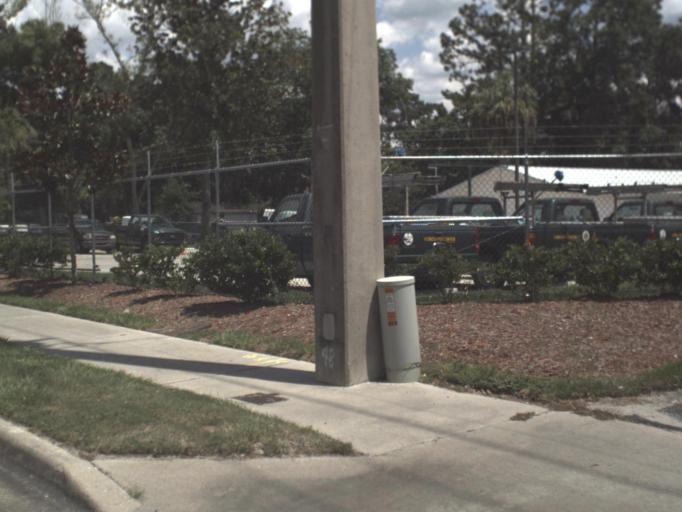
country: US
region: Florida
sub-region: Columbia County
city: Lake City
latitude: 30.1833
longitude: -82.6297
